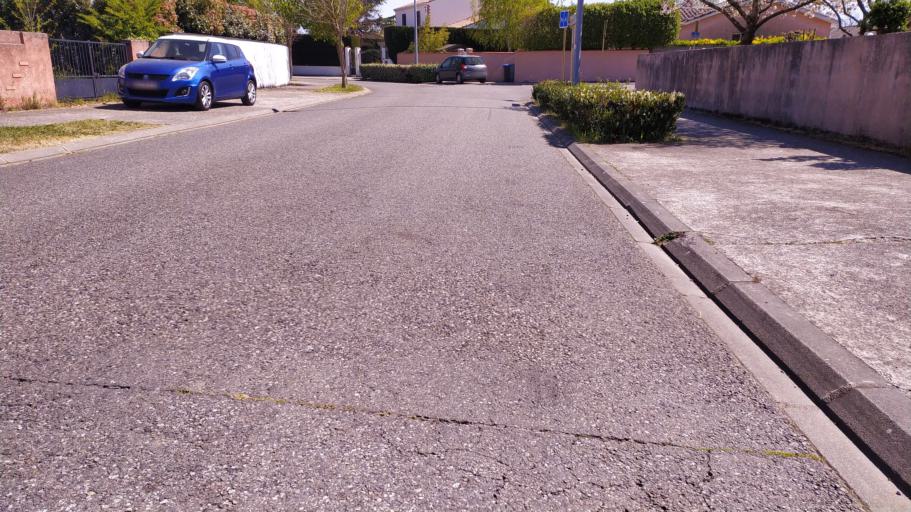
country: FR
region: Midi-Pyrenees
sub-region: Departement de la Haute-Garonne
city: Tournefeuille
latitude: 43.5887
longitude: 1.3132
